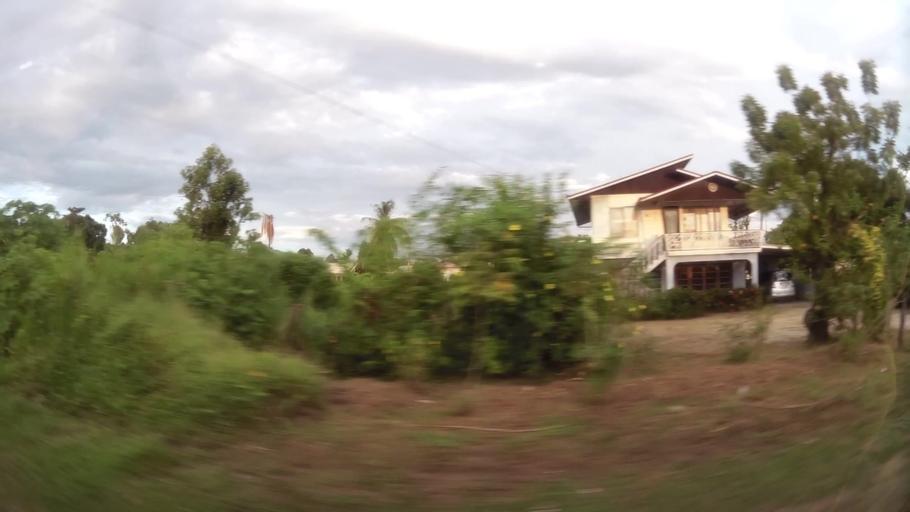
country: SR
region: Paramaribo
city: Paramaribo
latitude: 5.7814
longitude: -55.1665
